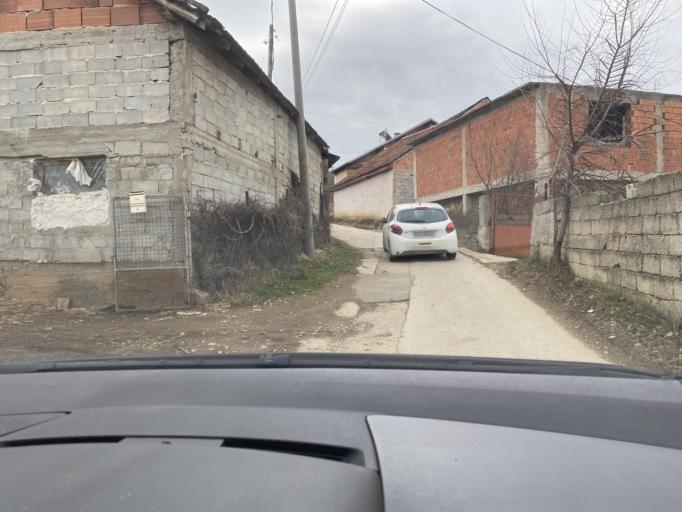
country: MK
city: Radishani
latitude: 42.1057
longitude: 21.4582
